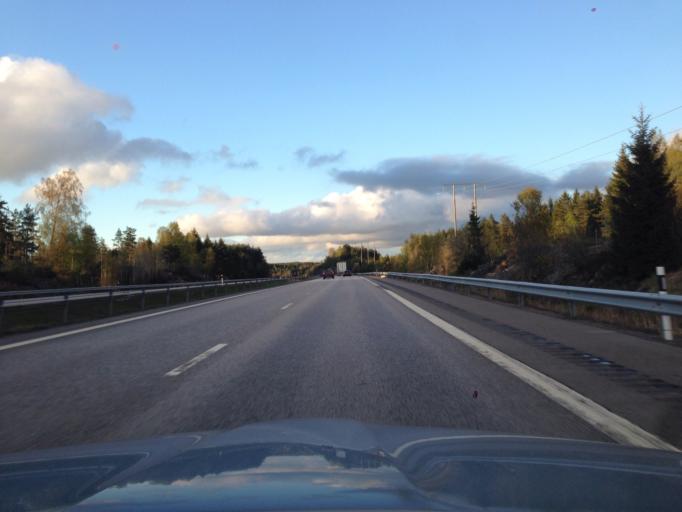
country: SE
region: Soedermanland
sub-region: Oxelosunds Kommun
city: Oxelosund
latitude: 58.8341
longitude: 17.1703
